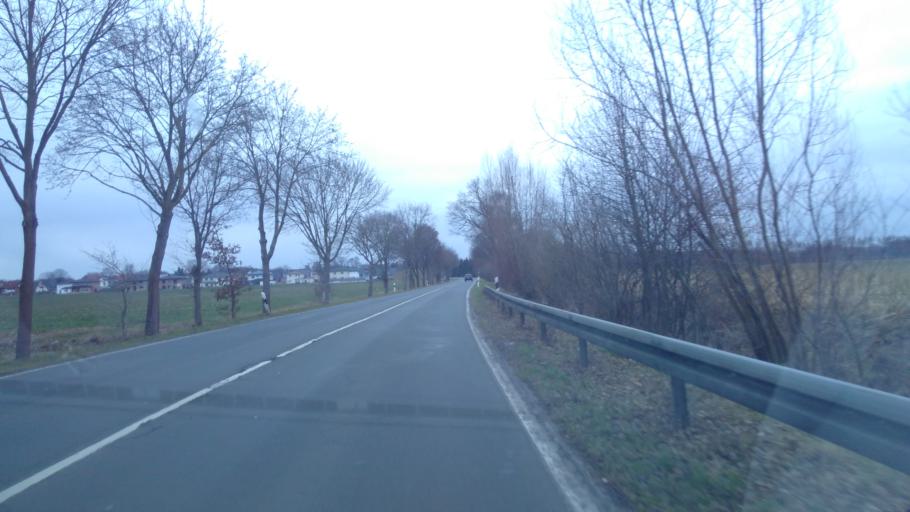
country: DE
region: North Rhine-Westphalia
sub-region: Regierungsbezirk Detmold
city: Delbruck
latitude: 51.7930
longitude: 8.5608
